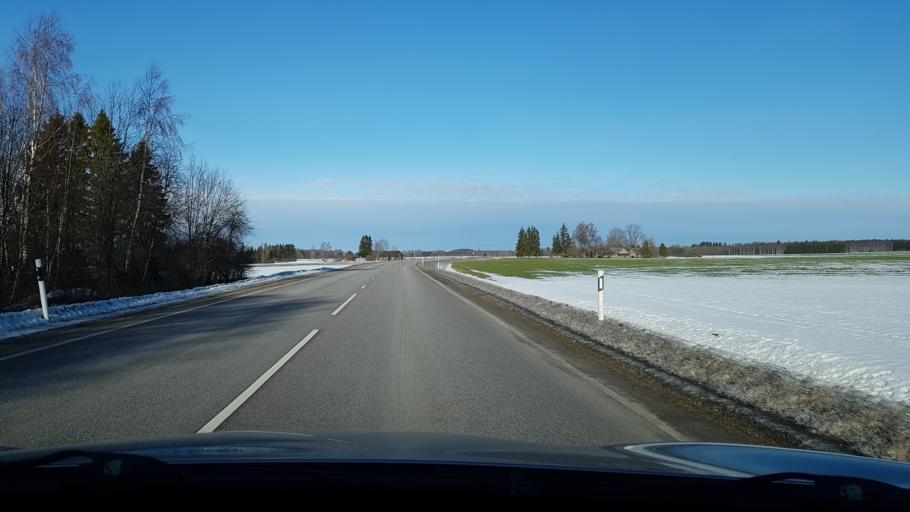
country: EE
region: Jogevamaa
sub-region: Poltsamaa linn
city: Poltsamaa
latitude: 58.6322
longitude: 25.7782
